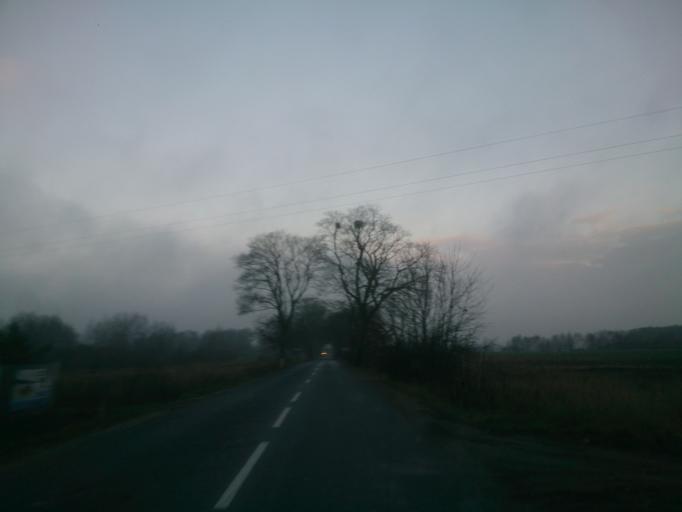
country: PL
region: Pomeranian Voivodeship
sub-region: Powiat starogardzki
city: Skorcz
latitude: 53.8239
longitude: 18.4631
